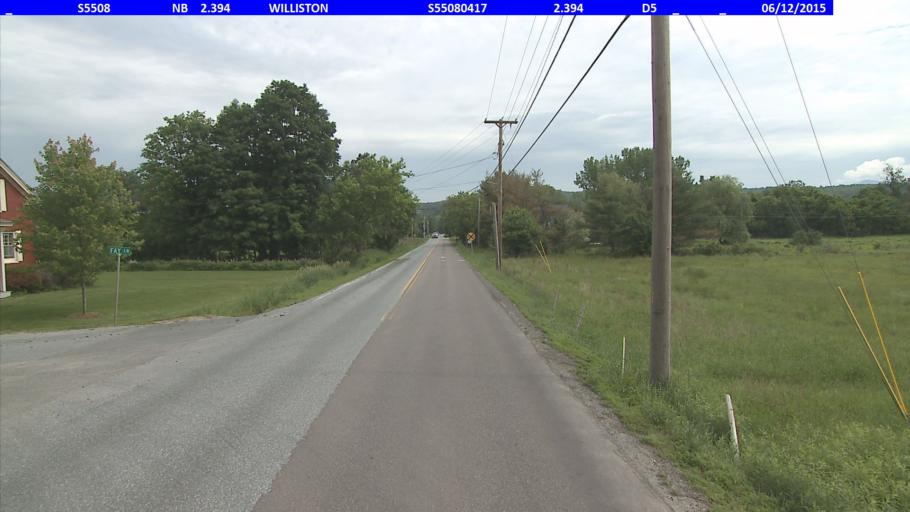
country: US
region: Vermont
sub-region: Chittenden County
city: Williston
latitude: 44.4652
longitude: -73.0477
